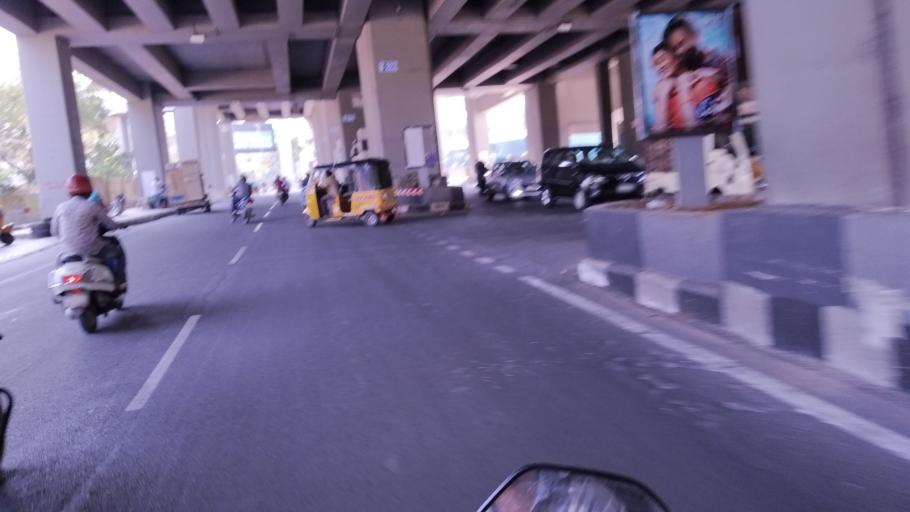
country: IN
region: Telangana
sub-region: Hyderabad
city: Malkajgiri
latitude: 17.4447
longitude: 78.4975
